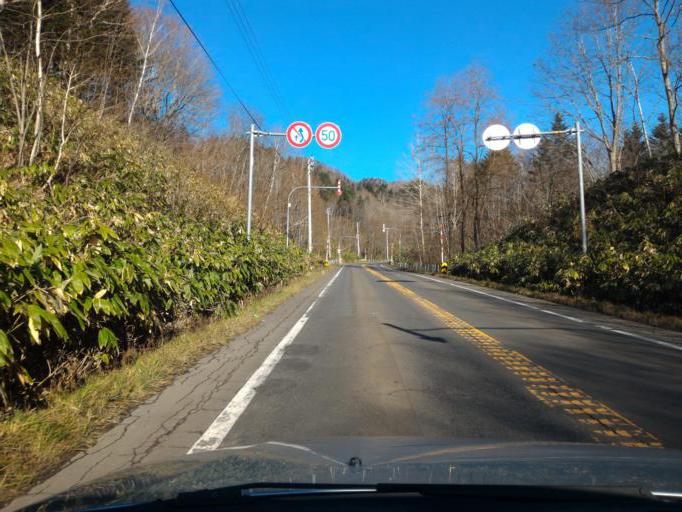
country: JP
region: Hokkaido
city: Bibai
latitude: 43.2643
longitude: 142.0318
